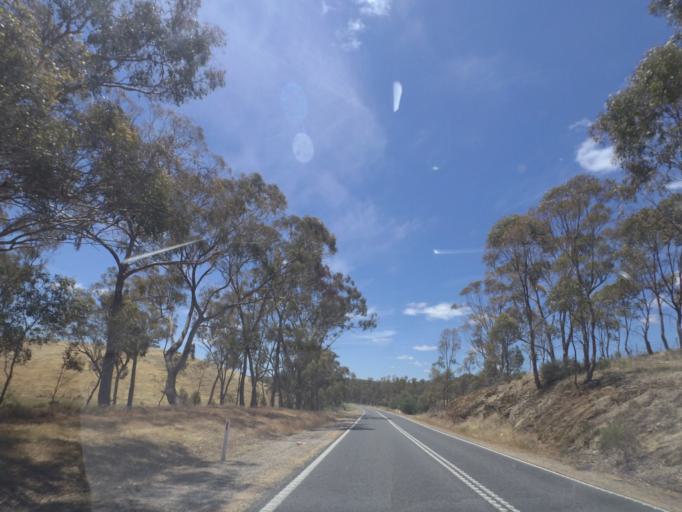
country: AU
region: Victoria
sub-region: Mount Alexander
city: Castlemaine
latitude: -37.2016
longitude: 144.1438
